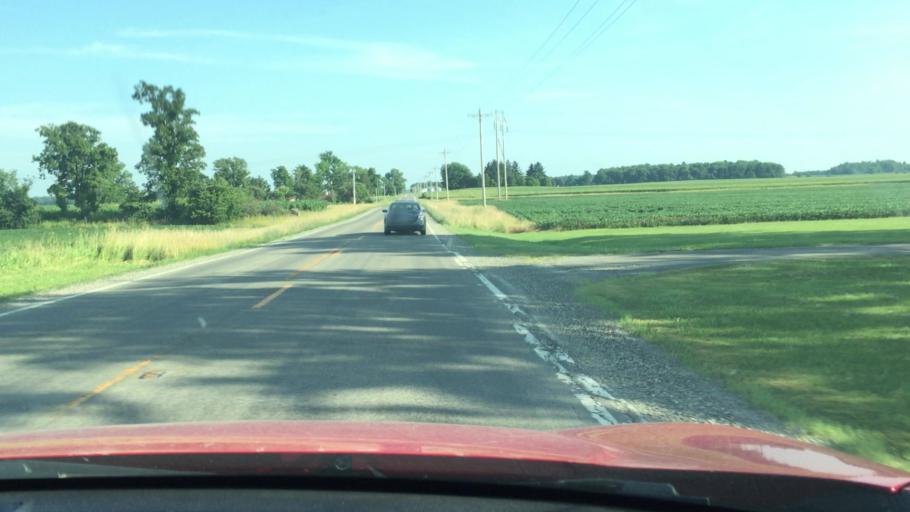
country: US
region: Ohio
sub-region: Hardin County
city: Ada
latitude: 40.6702
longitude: -83.8548
